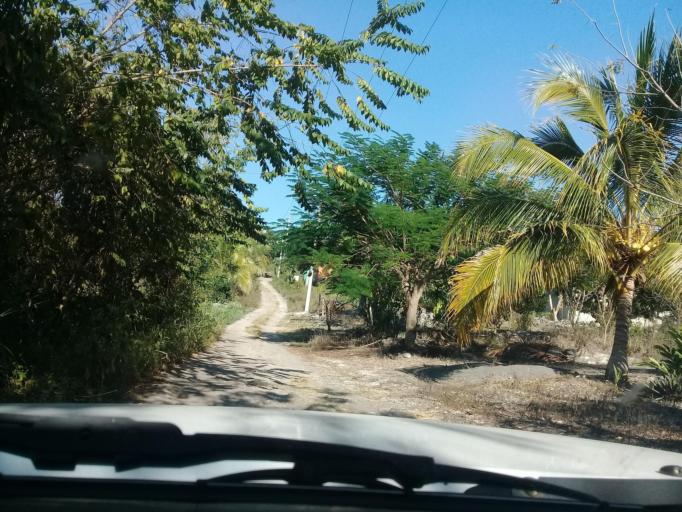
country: MX
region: Veracruz
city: Rinconada
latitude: 19.4004
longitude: -96.5616
